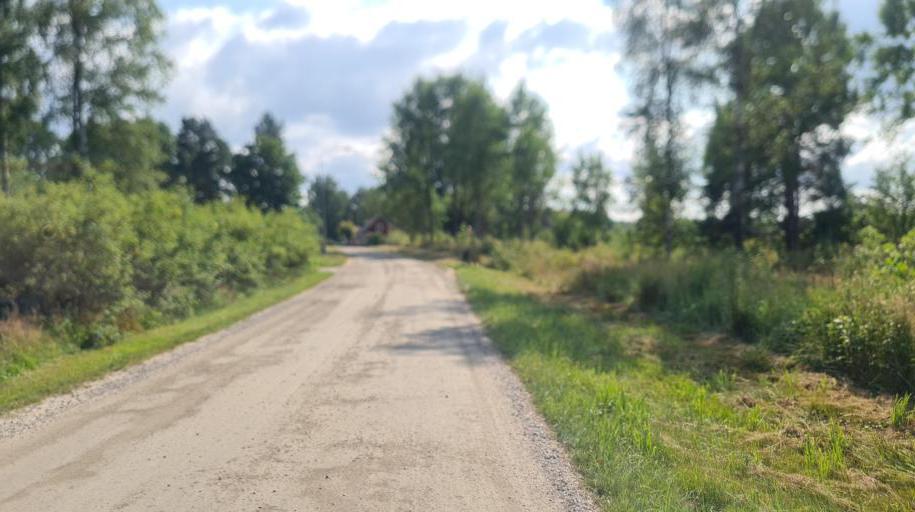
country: SE
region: Kronoberg
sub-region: Ljungby Kommun
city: Ljungby
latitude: 56.7375
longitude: 13.8734
